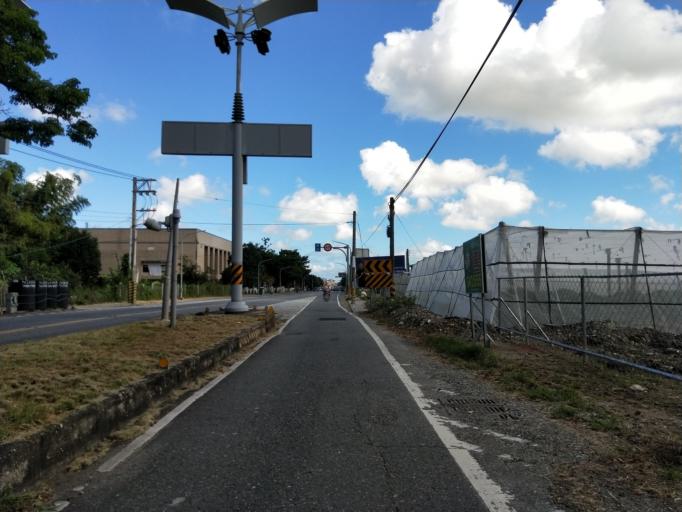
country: TW
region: Taiwan
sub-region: Taitung
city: Taitung
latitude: 22.7896
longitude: 121.1101
